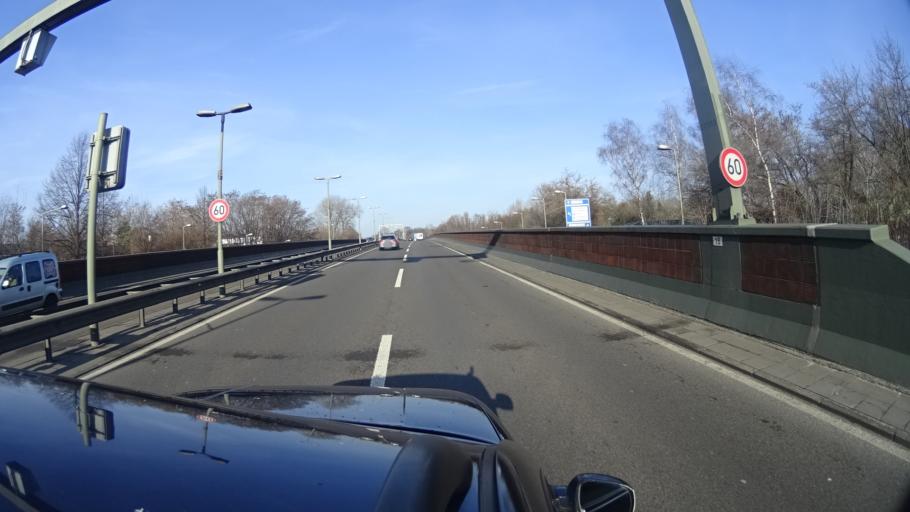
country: DE
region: Berlin
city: Tegel
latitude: 52.5938
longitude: 13.2865
